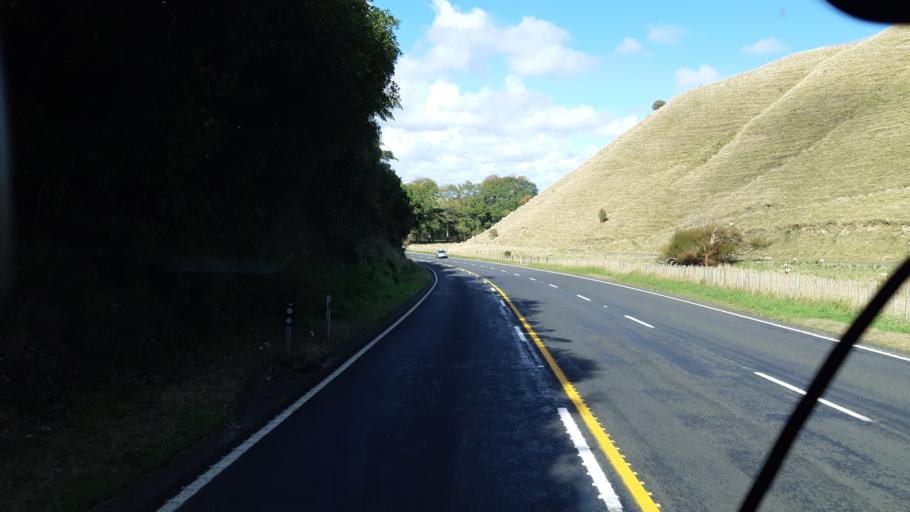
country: NZ
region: Manawatu-Wanganui
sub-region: Wanganui District
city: Wanganui
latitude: -40.0309
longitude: 175.2042
